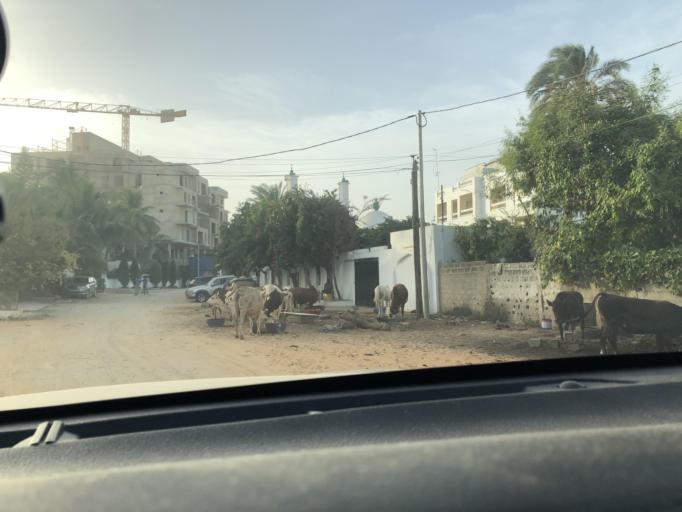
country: SN
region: Dakar
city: Mermoz Boabab
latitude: 14.7423
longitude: -17.5158
